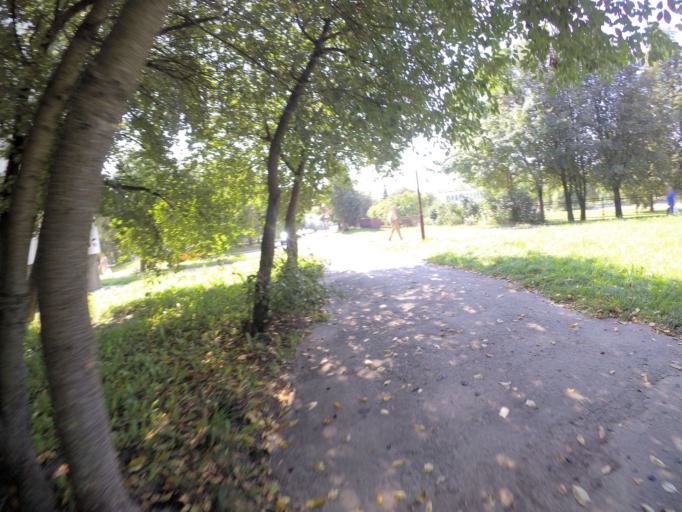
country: BY
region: Grodnenskaya
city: Hrodna
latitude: 53.7038
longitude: 23.8459
